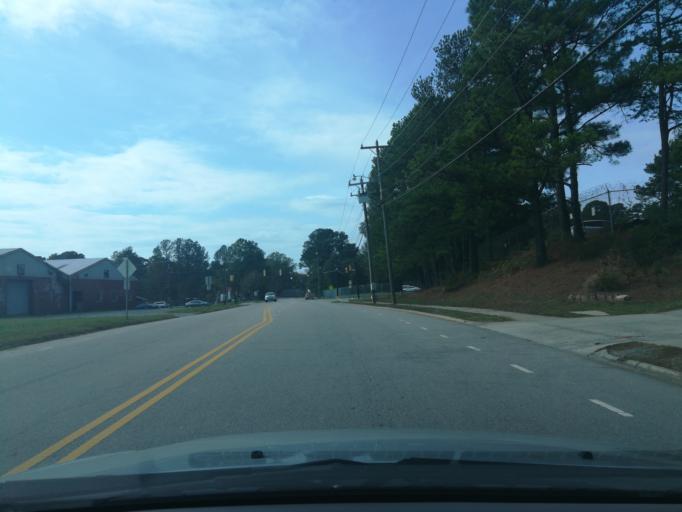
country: US
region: North Carolina
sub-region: Durham County
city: Durham
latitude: 35.9743
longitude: -78.8838
